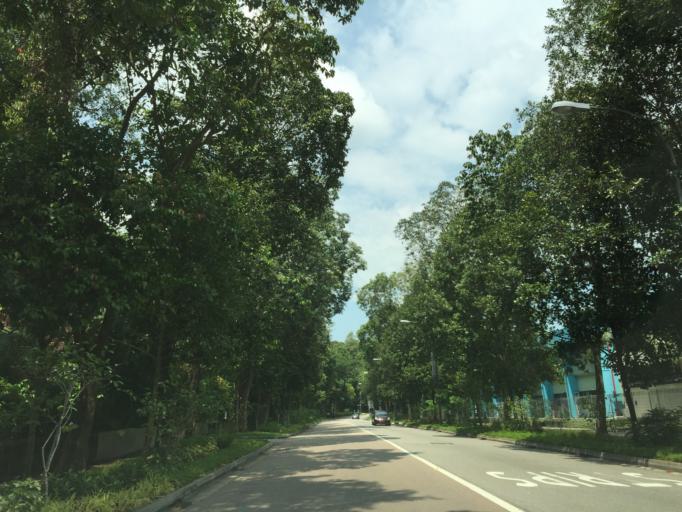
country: SG
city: Singapore
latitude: 1.3179
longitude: 103.8196
